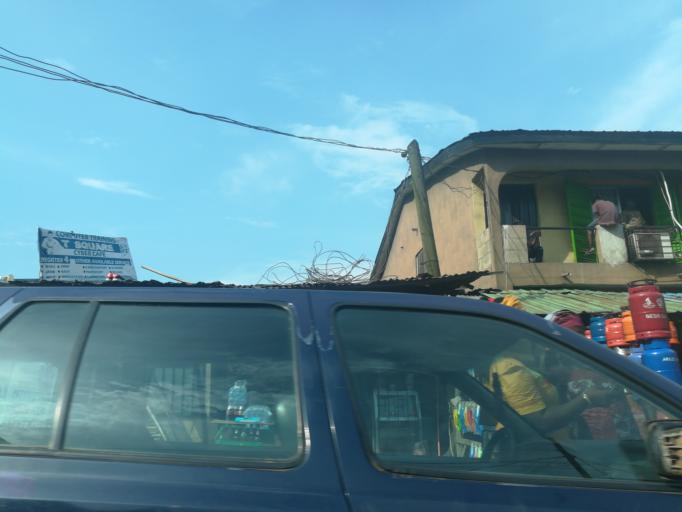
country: NG
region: Lagos
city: Ikorodu
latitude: 6.6221
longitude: 3.5019
